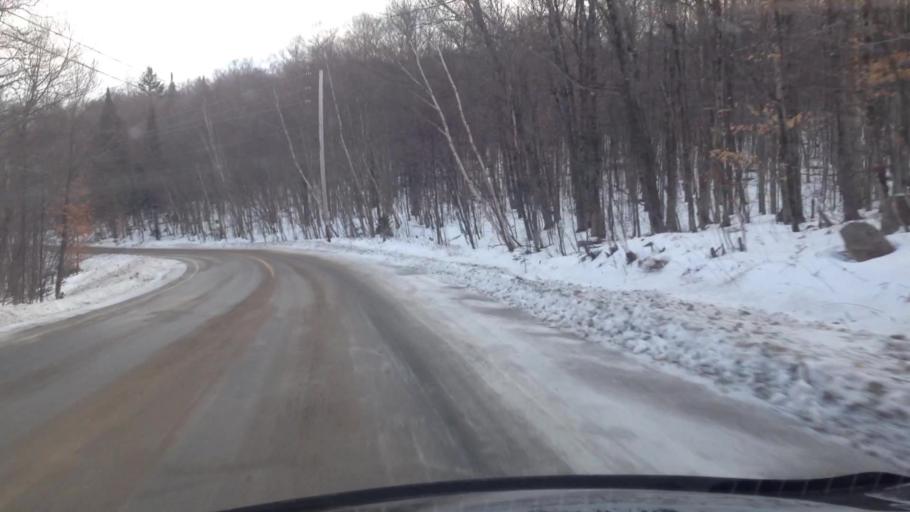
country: CA
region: Quebec
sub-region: Laurentides
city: Sainte-Agathe-des-Monts
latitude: 45.9219
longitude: -74.4978
